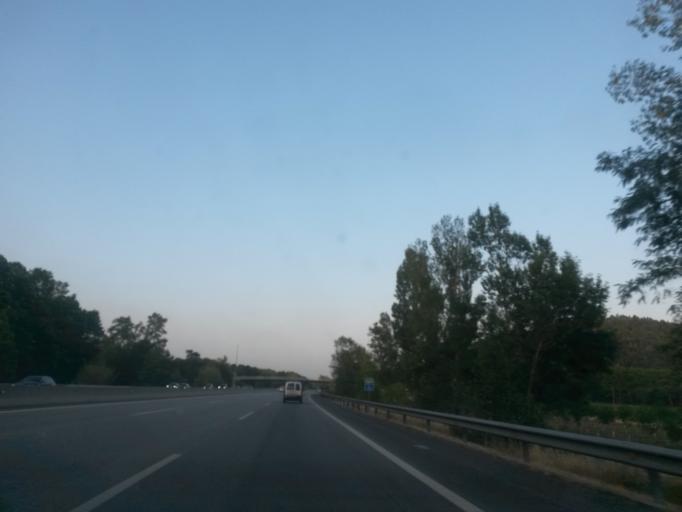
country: ES
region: Catalonia
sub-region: Provincia de Girona
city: Breda
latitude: 41.7246
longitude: 2.5830
